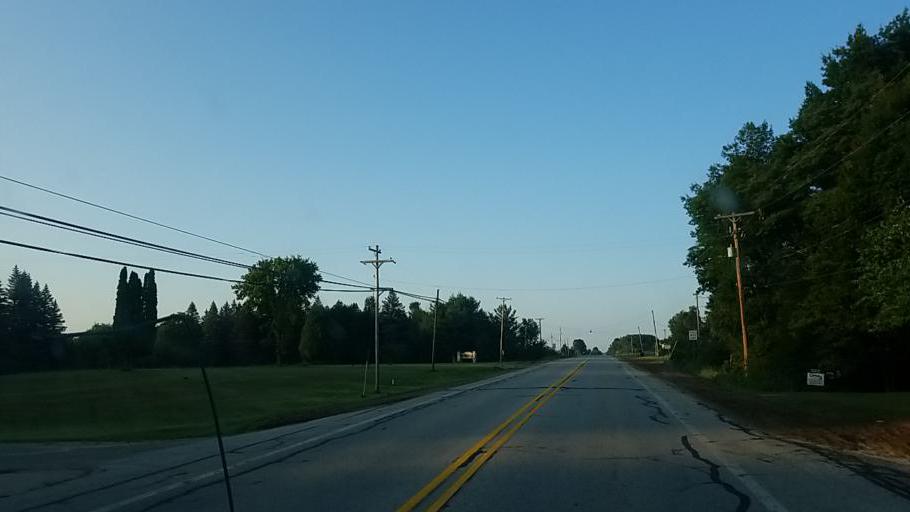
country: US
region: Michigan
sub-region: Isabella County
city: Lake Isabella
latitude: 43.7447
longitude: -85.1474
